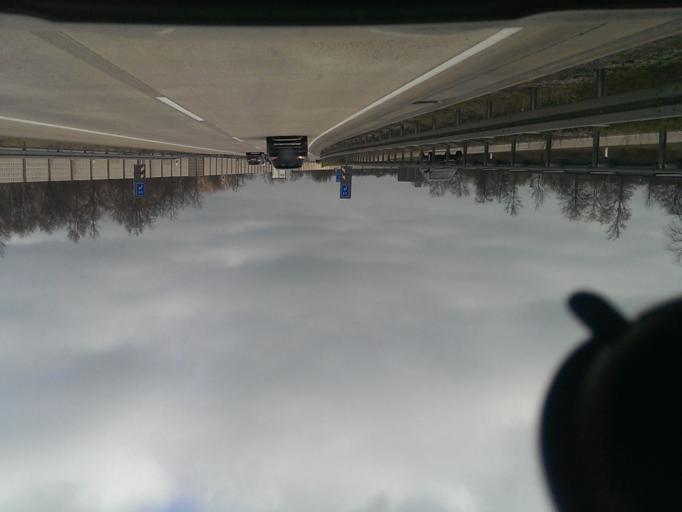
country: DE
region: Lower Saxony
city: Langenhagen
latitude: 52.4491
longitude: 9.7195
